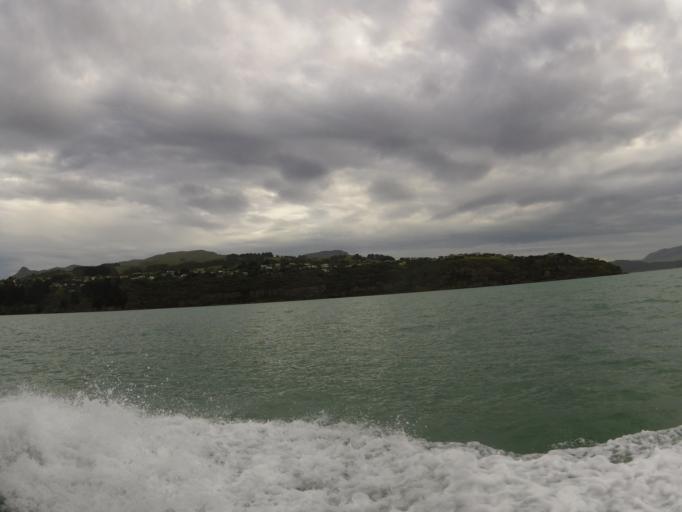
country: NZ
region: Canterbury
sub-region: Christchurch City
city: Christchurch
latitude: -43.6184
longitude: 172.7275
